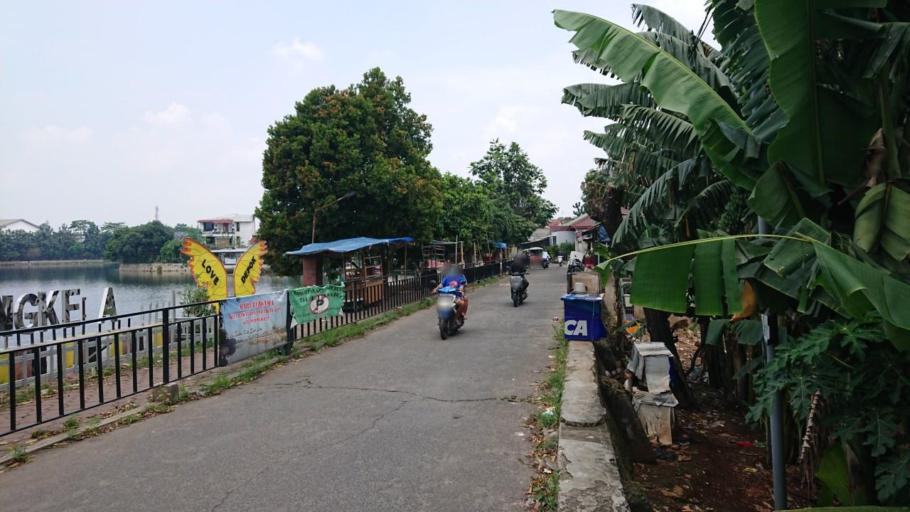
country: ID
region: West Java
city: Depok
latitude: -6.3480
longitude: 106.8564
